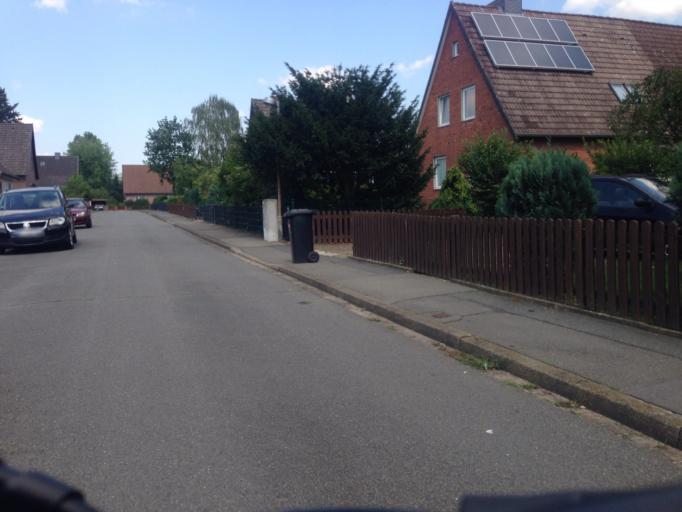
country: DE
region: Lower Saxony
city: Adendorf
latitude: 53.2832
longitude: 10.4362
